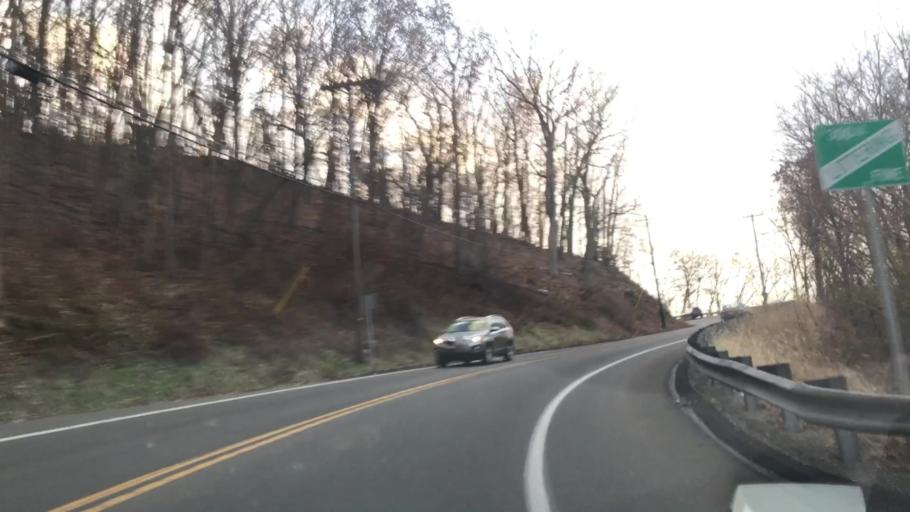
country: US
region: Pennsylvania
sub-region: Allegheny County
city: Carnot-Moon
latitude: 40.5277
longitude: -80.2290
